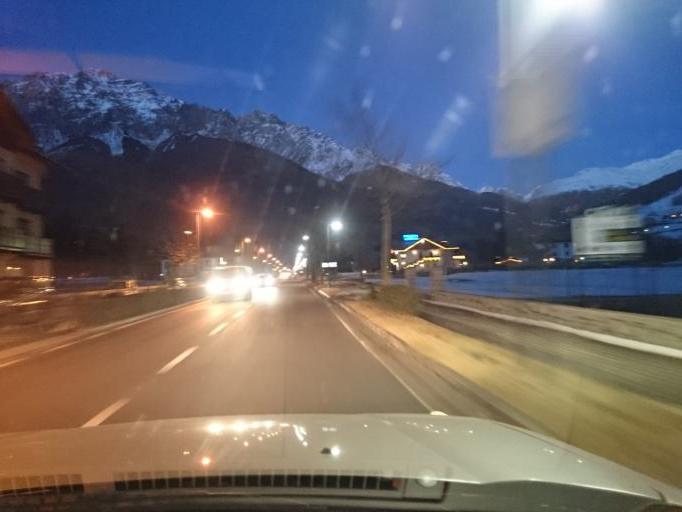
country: IT
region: Lombardy
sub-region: Provincia di Sondrio
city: Bormio
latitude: 46.4613
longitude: 10.3606
